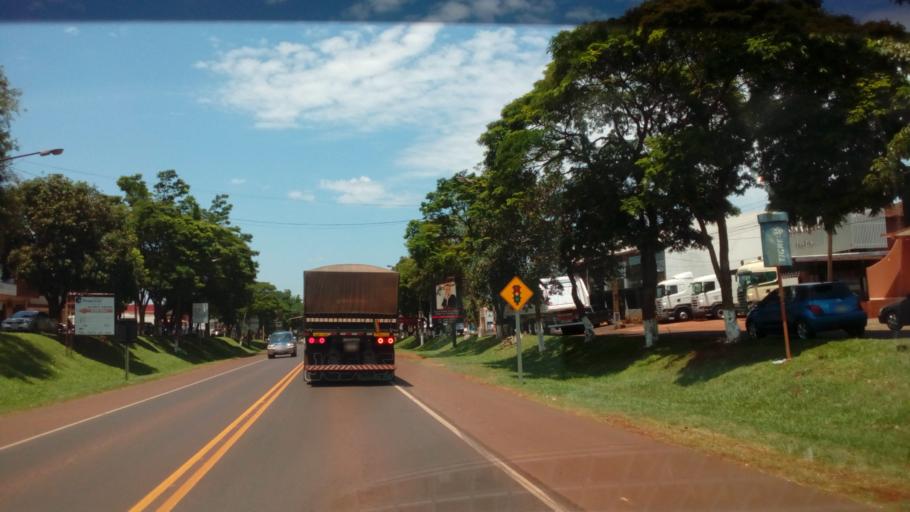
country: PY
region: Alto Parana
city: Santa Rita
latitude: -25.8015
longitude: -55.0935
